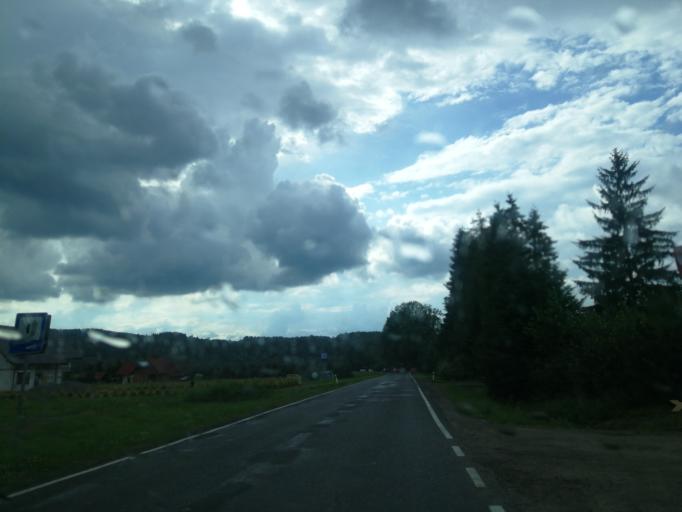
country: PL
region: Subcarpathian Voivodeship
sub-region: Powiat leski
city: Uherce Mineralne
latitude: 49.4595
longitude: 22.4075
